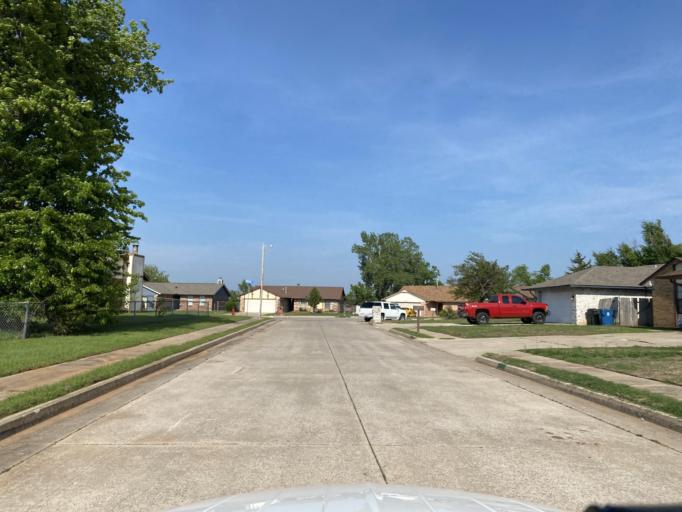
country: US
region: Oklahoma
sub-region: Oklahoma County
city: Spencer
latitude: 35.4900
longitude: -97.3742
